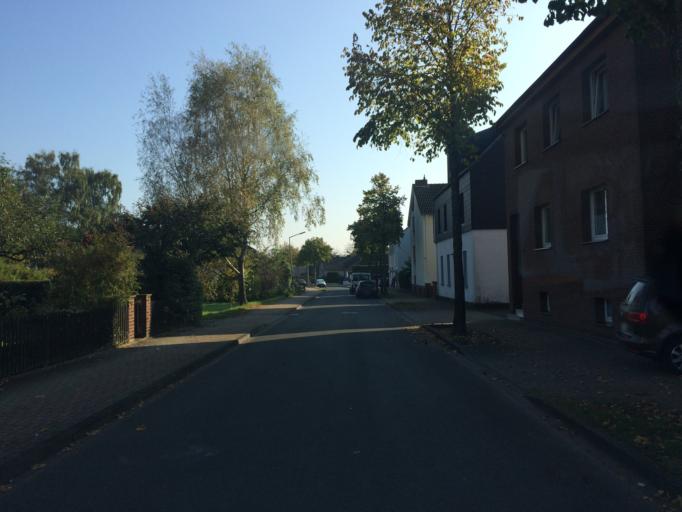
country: DE
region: North Rhine-Westphalia
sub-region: Regierungsbezirk Munster
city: Ennigerloh
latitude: 51.8018
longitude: 8.0177
